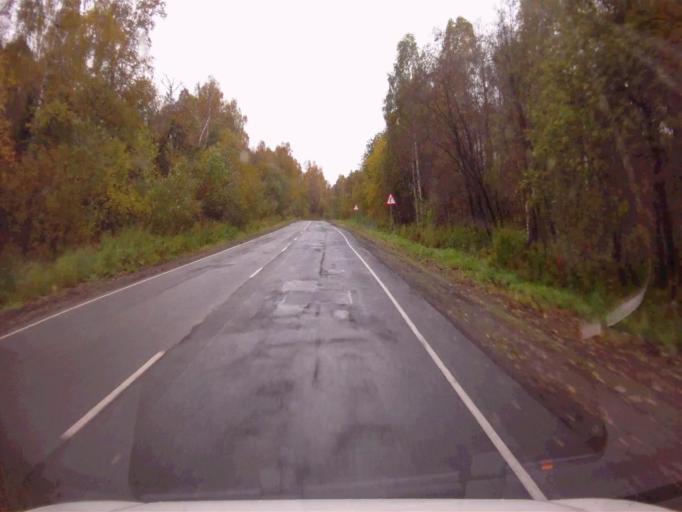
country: RU
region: Chelyabinsk
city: Nizhniy Ufaley
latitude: 56.0548
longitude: 60.0432
